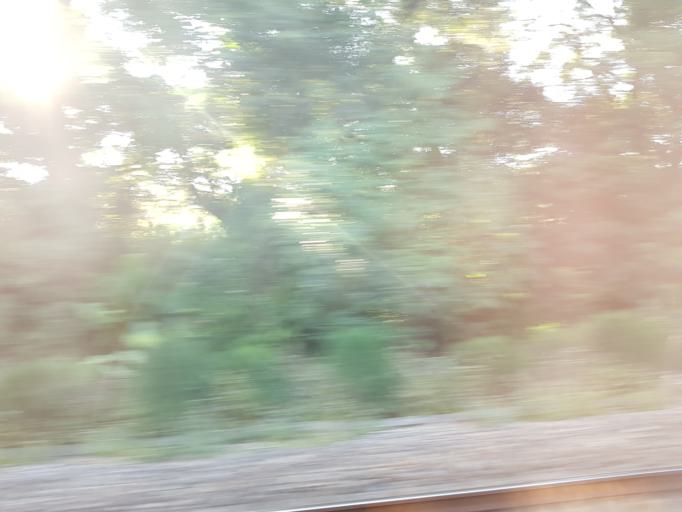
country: TW
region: Taiwan
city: Fengyuan
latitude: 24.2958
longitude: 120.7326
